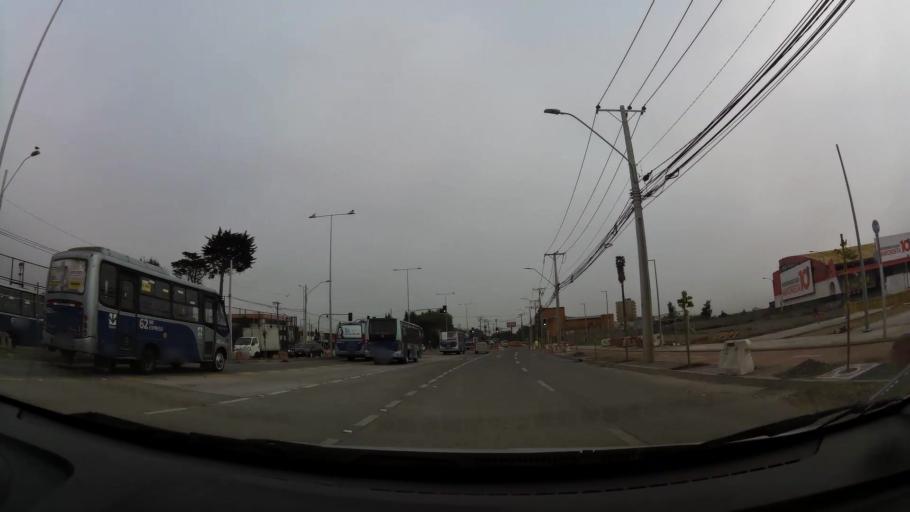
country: CL
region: Biobio
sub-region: Provincia de Concepcion
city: Concepcion
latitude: -36.7995
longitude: -73.0850
